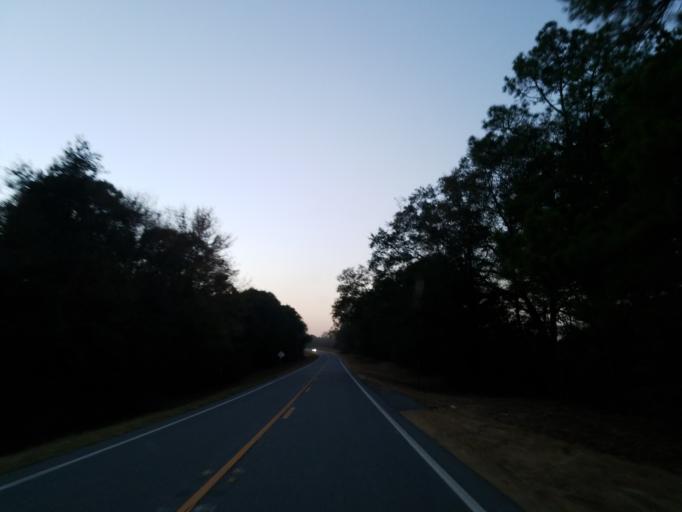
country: US
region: Georgia
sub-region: Wilcox County
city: Rochelle
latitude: 31.8144
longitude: -83.5059
